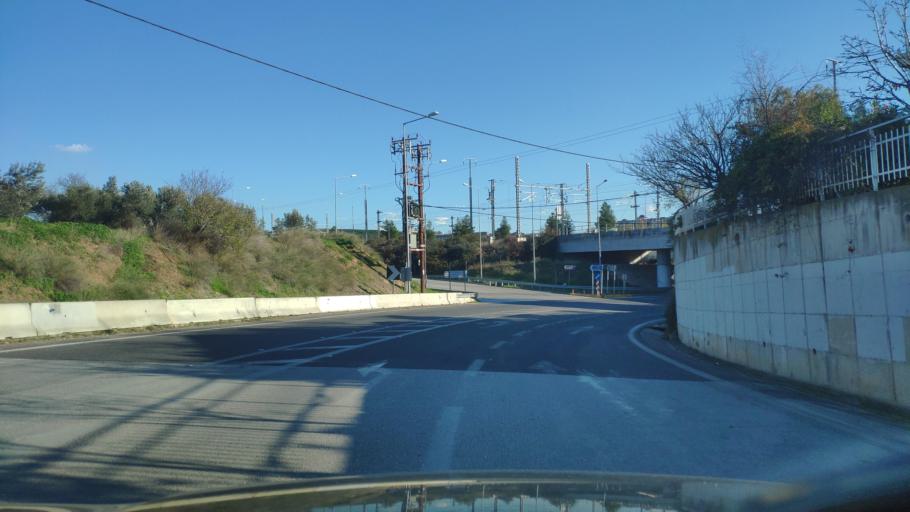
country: GR
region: Peloponnese
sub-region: Nomos Korinthias
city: Korinthos
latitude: 37.9223
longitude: 22.9367
